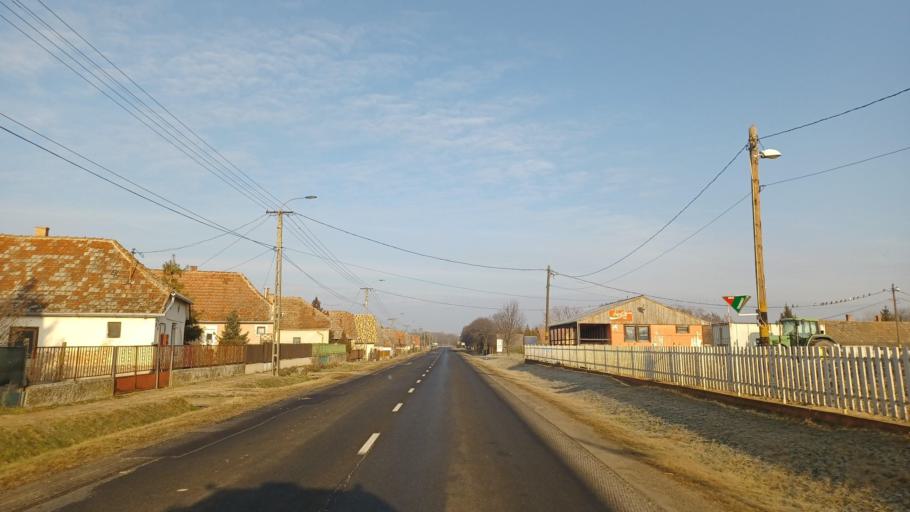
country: HU
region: Fejer
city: Cece
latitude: 46.7209
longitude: 18.6627
